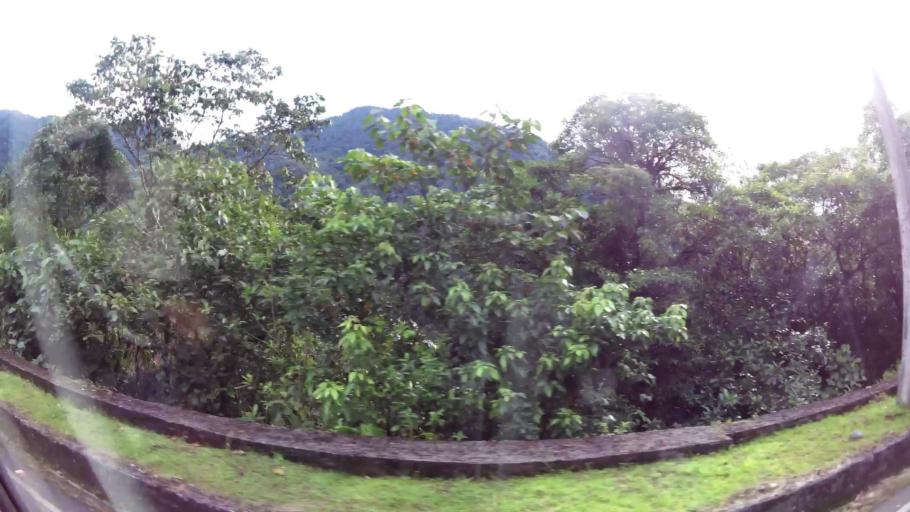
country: EC
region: Pastaza
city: Puyo
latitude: -1.4485
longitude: -78.1741
